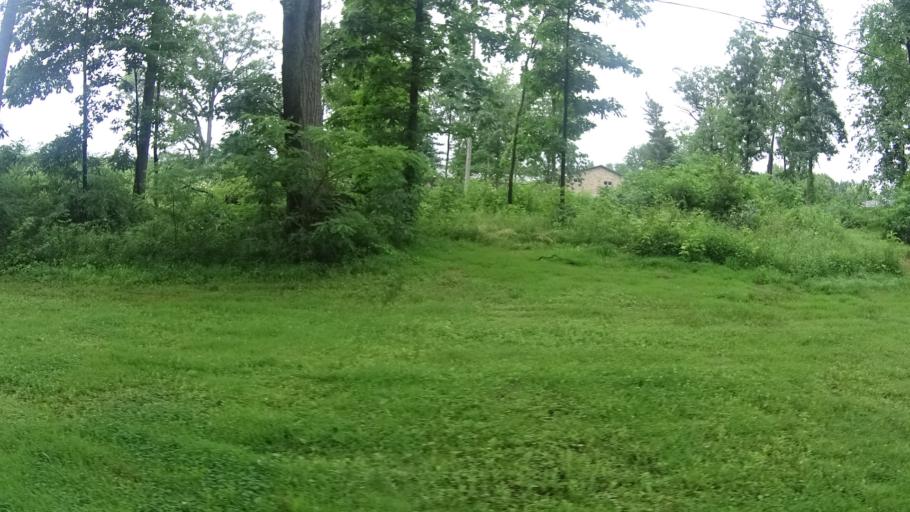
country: US
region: Ohio
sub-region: Erie County
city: Huron
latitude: 41.3266
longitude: -82.4877
